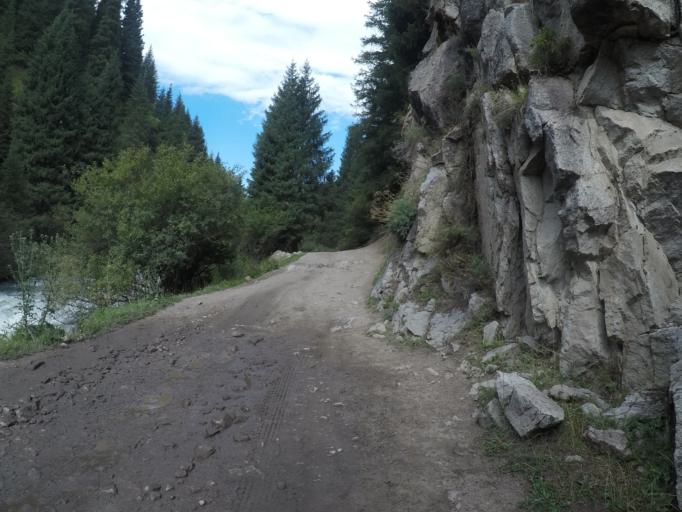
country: KG
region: Ysyk-Koel
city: Teploklyuchenka
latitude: 42.4420
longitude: 78.5547
